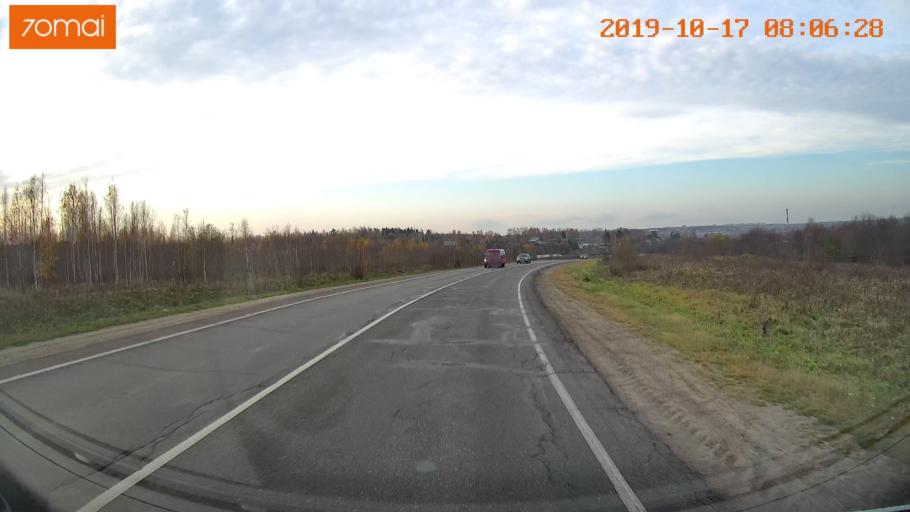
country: RU
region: Vladimir
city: Kol'chugino
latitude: 56.3224
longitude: 39.4133
